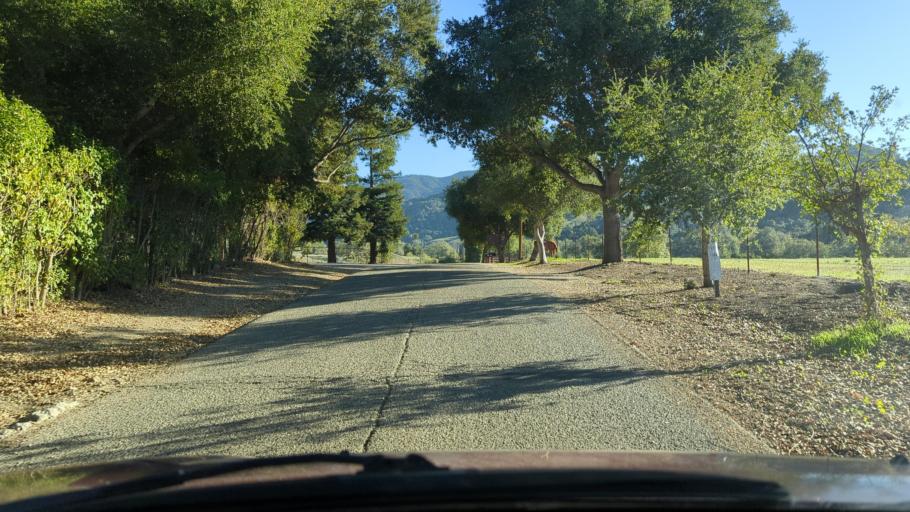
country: US
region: California
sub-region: Santa Barbara County
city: Santa Ynez
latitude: 34.5754
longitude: -120.0983
